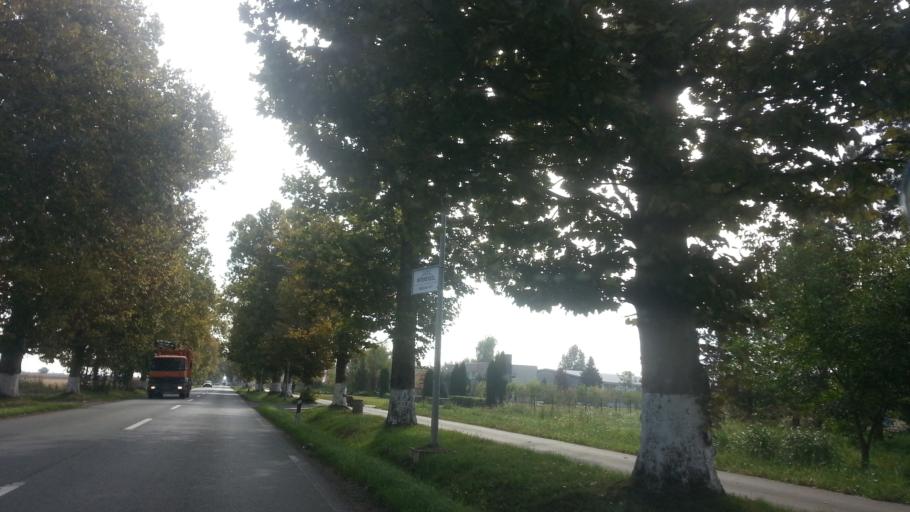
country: RS
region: Autonomna Pokrajina Vojvodina
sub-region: Sremski Okrug
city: Stara Pazova
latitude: 44.9729
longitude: 20.1736
